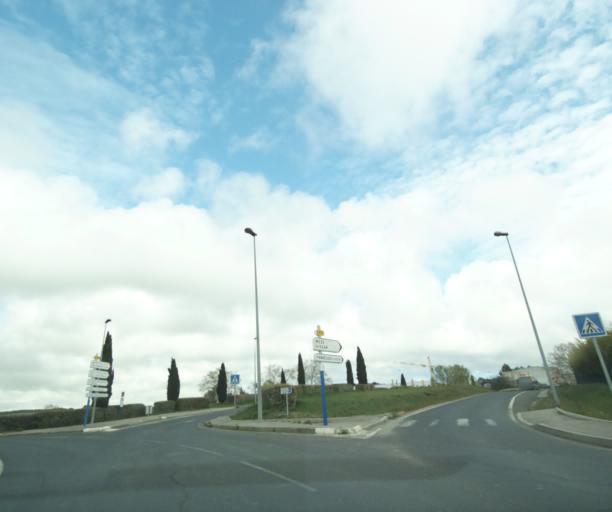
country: FR
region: Languedoc-Roussillon
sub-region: Departement de l'Herault
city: Fabregues
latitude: 43.5601
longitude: 3.7964
